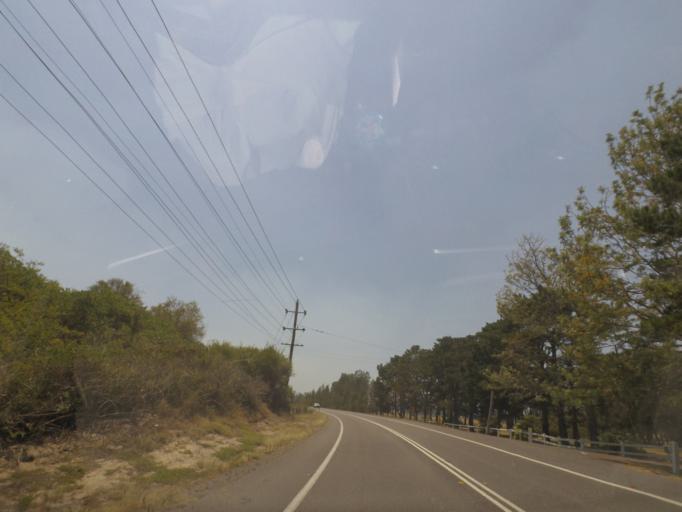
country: AU
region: New South Wales
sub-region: Port Stephens Shire
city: Medowie
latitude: -32.8070
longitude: 151.8736
